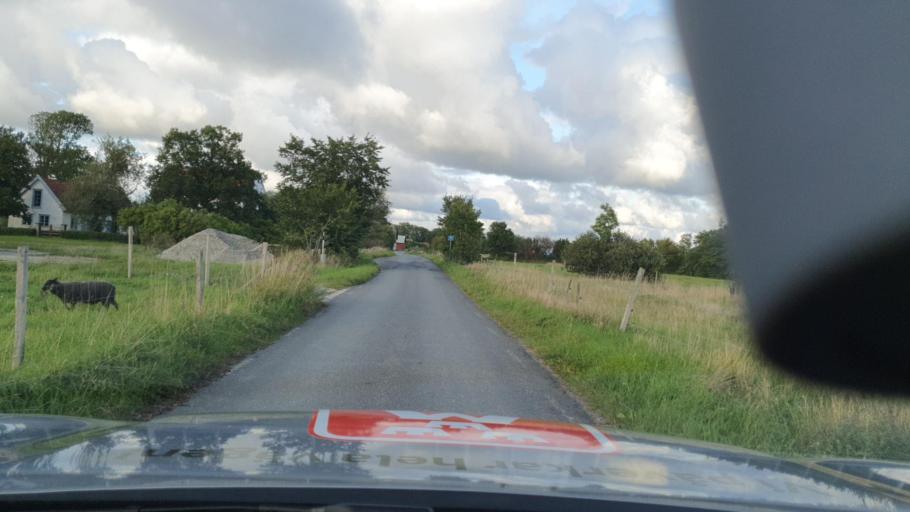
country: SE
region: Gotland
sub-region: Gotland
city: Hemse
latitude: 57.2218
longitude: 18.2370
